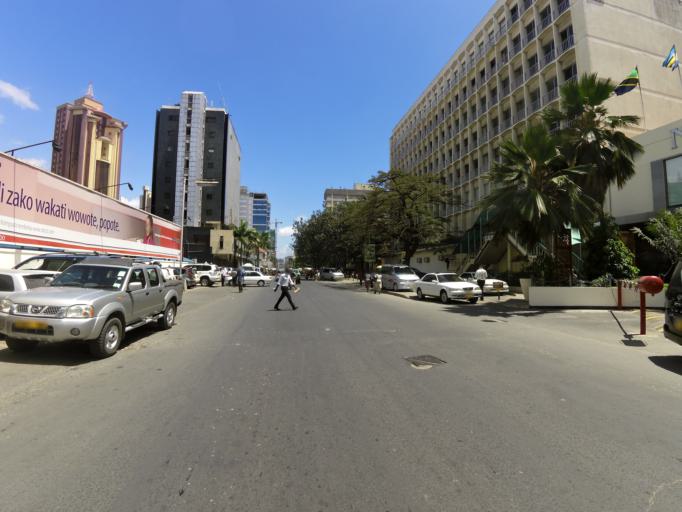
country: TZ
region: Dar es Salaam
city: Dar es Salaam
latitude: -6.8174
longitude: 39.2903
